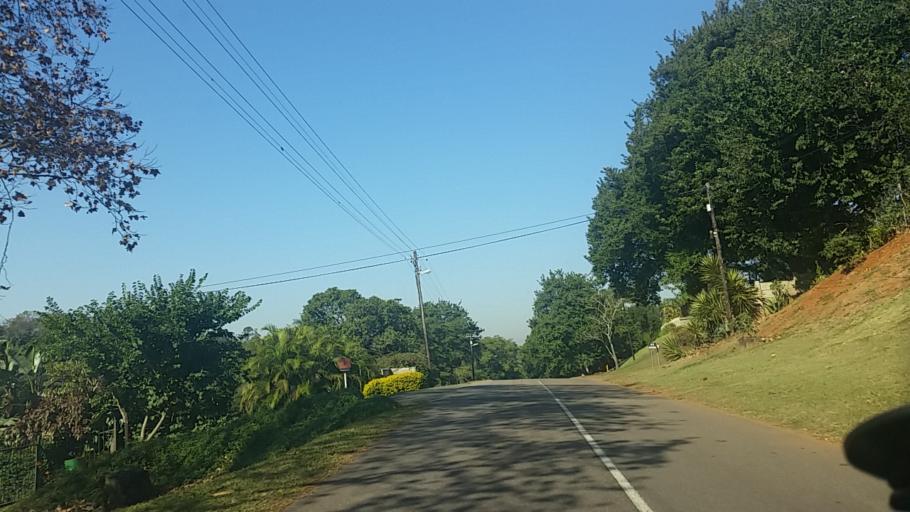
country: ZA
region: KwaZulu-Natal
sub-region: eThekwini Metropolitan Municipality
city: Berea
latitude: -29.8522
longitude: 30.9053
